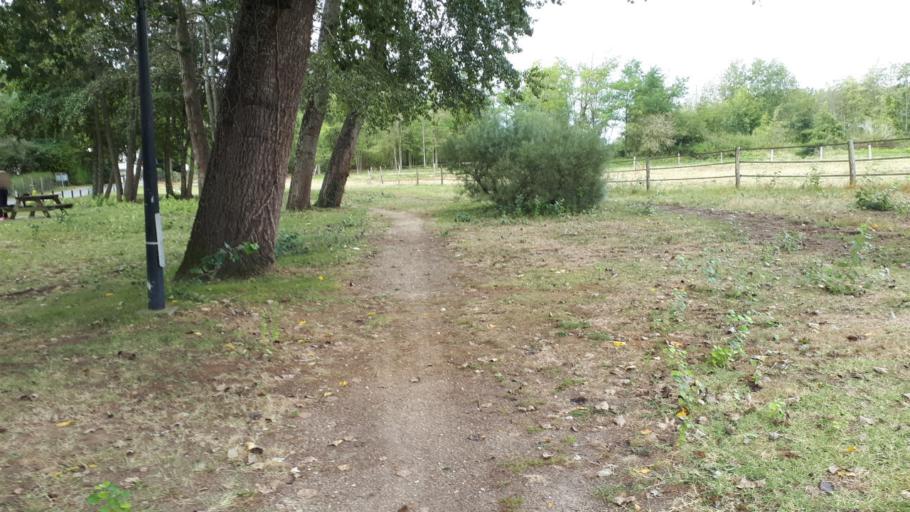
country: FR
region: Centre
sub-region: Departement du Loir-et-Cher
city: Saint-Gervais-la-Foret
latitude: 47.5680
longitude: 1.3439
